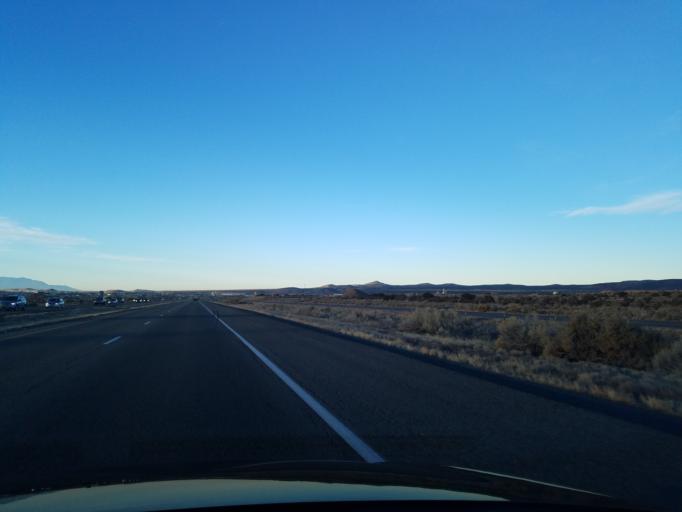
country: US
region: New Mexico
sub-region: Santa Fe County
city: Agua Fria
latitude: 35.6457
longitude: -106.0579
